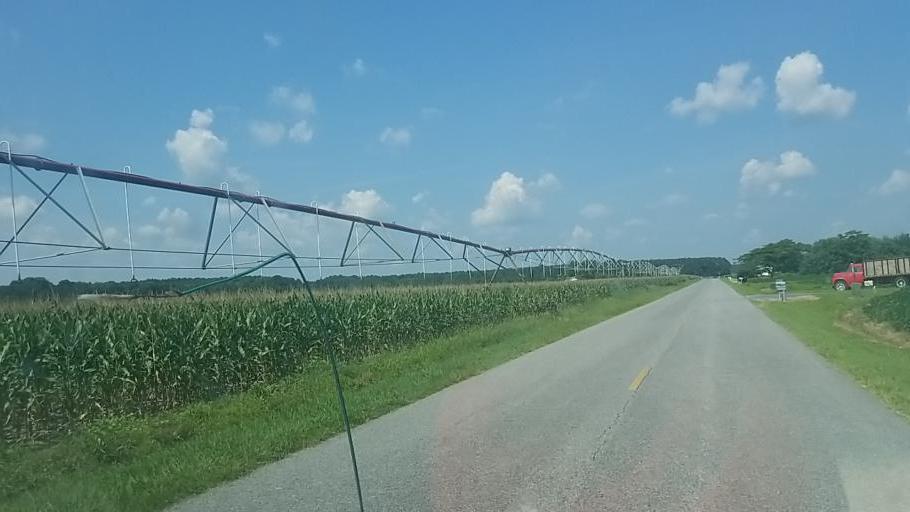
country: US
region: Maryland
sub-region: Worcester County
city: Berlin
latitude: 38.2956
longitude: -75.2594
